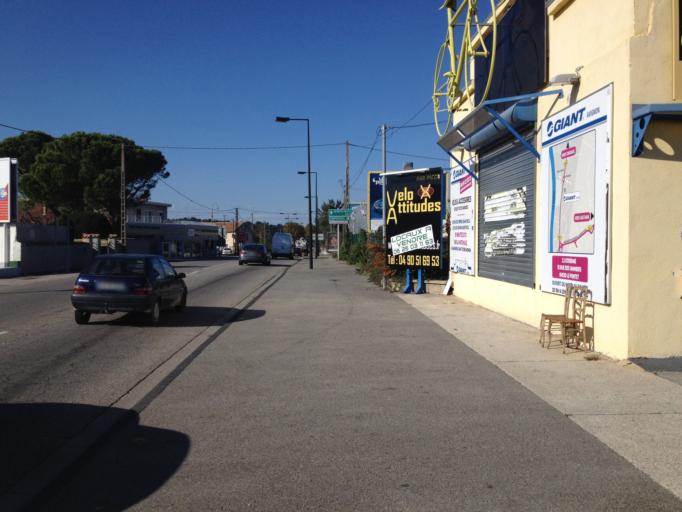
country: FR
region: Provence-Alpes-Cote d'Azur
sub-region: Departement du Vaucluse
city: Orange
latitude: 44.1240
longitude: 4.8277
